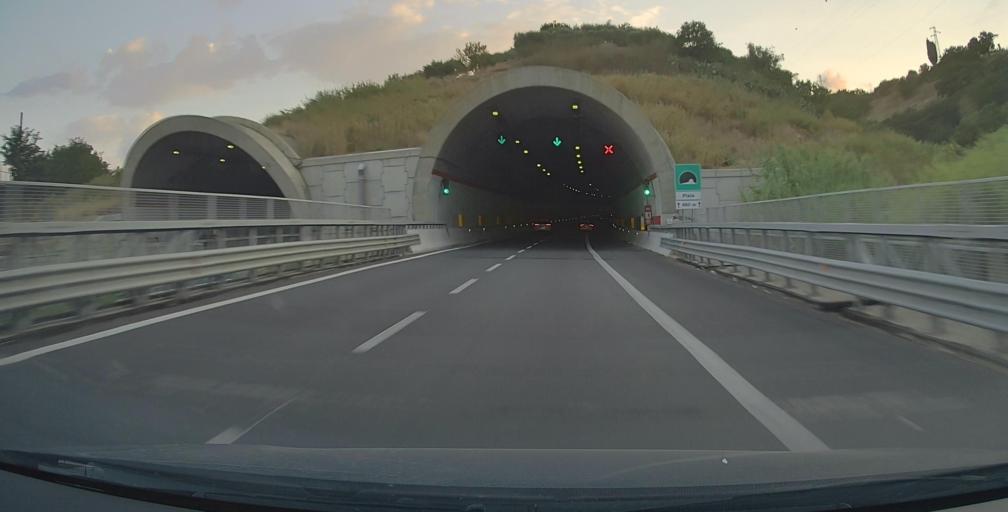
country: IT
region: Calabria
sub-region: Provincia di Reggio Calabria
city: Campo Calabro
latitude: 38.2212
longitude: 15.6482
